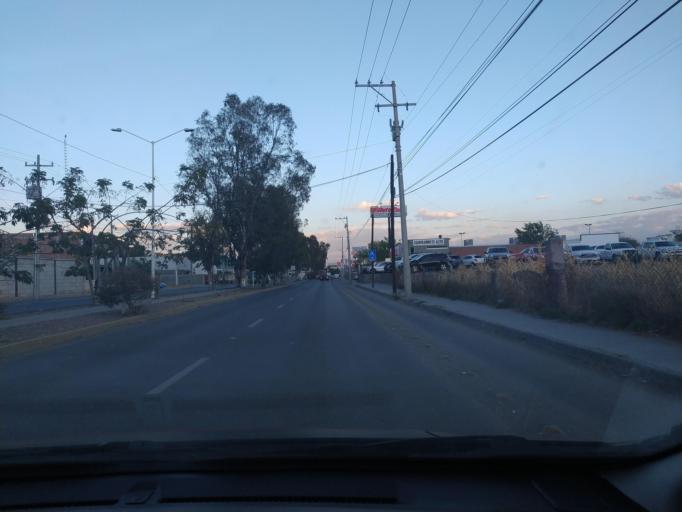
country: LA
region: Oudomxai
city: Muang La
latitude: 21.0287
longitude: 101.8649
